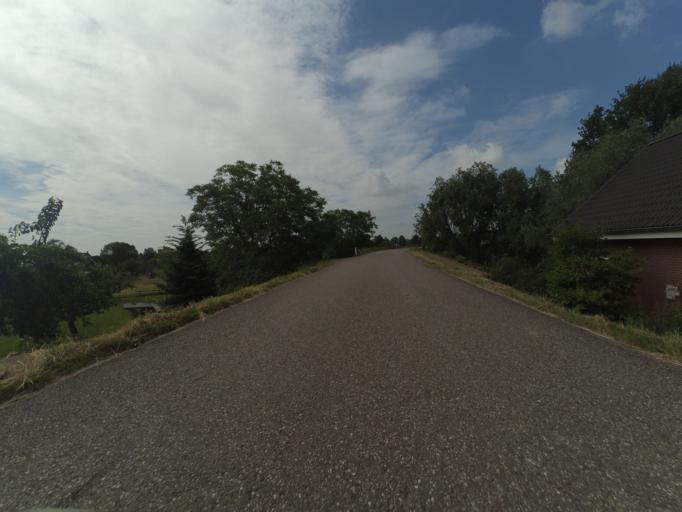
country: NL
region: Utrecht
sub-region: Gemeente Rhenen
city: Rhenen
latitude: 51.9374
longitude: 5.5784
